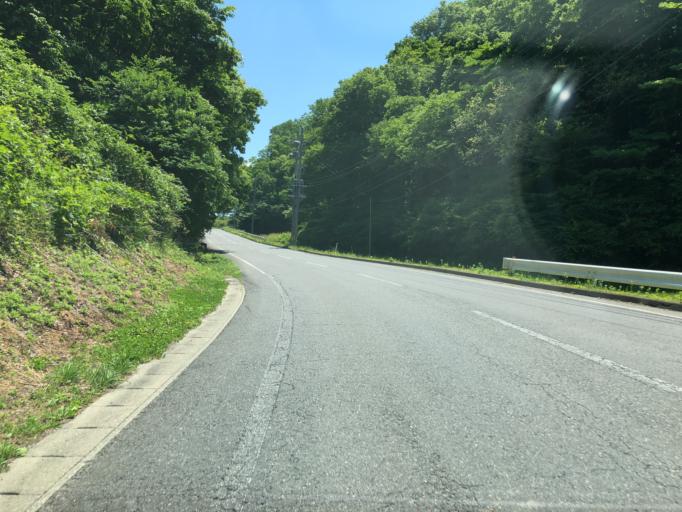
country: JP
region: Fukushima
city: Funehikimachi-funehiki
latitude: 37.4845
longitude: 140.5575
